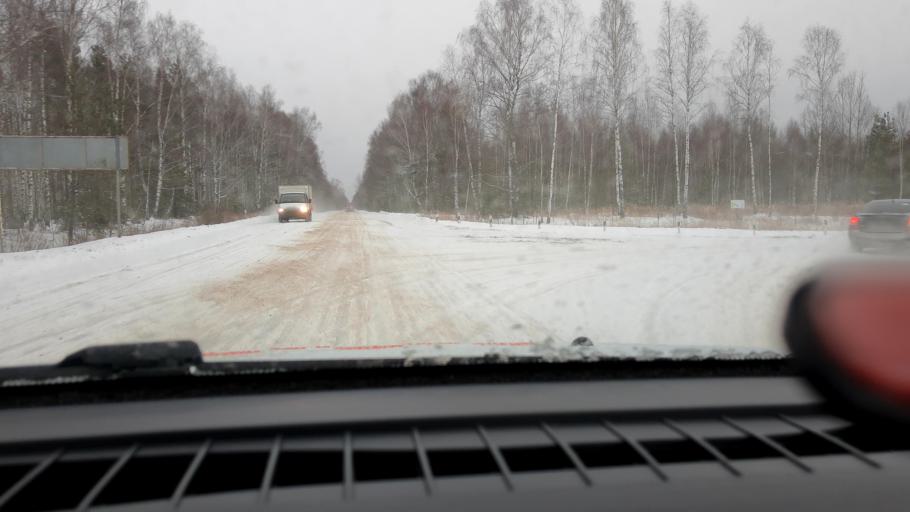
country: RU
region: Nizjnij Novgorod
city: Pamyat' Parizhskoy Kommuny
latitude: 56.2417
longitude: 44.4967
